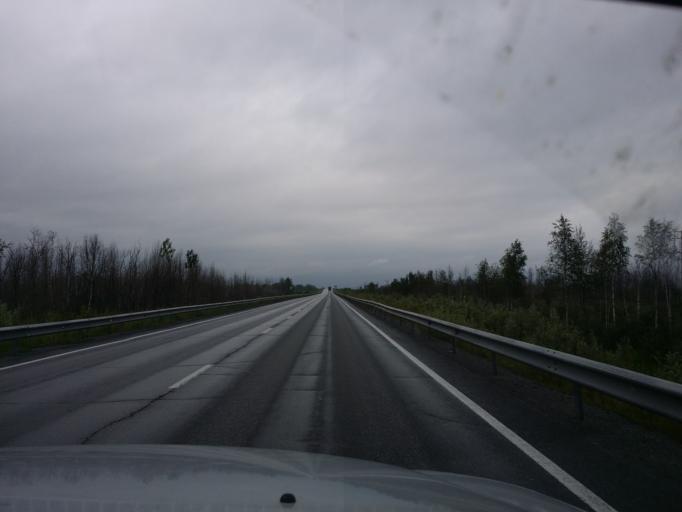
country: RU
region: Khanty-Mansiyskiy Avtonomnyy Okrug
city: Lokosovo
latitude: 61.4541
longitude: 74.6873
